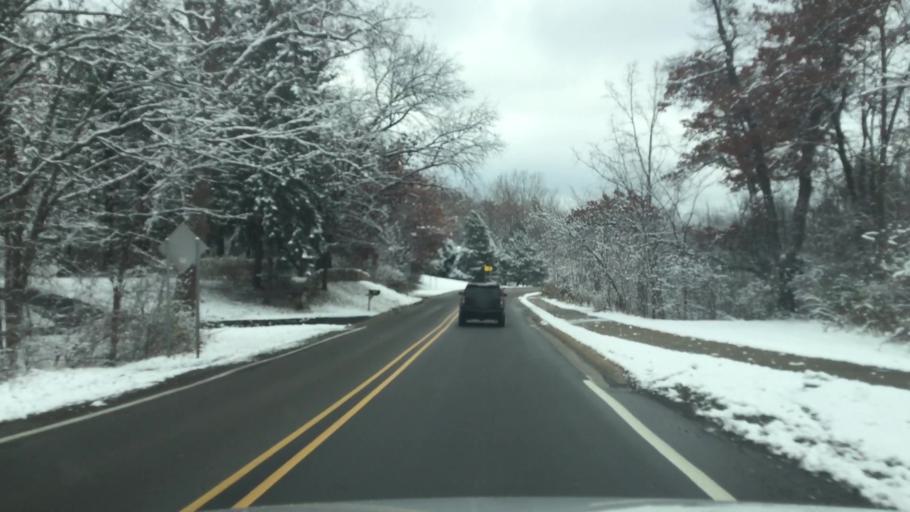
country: US
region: Michigan
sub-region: Oakland County
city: West Bloomfield Township
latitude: 42.5690
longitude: -83.4146
